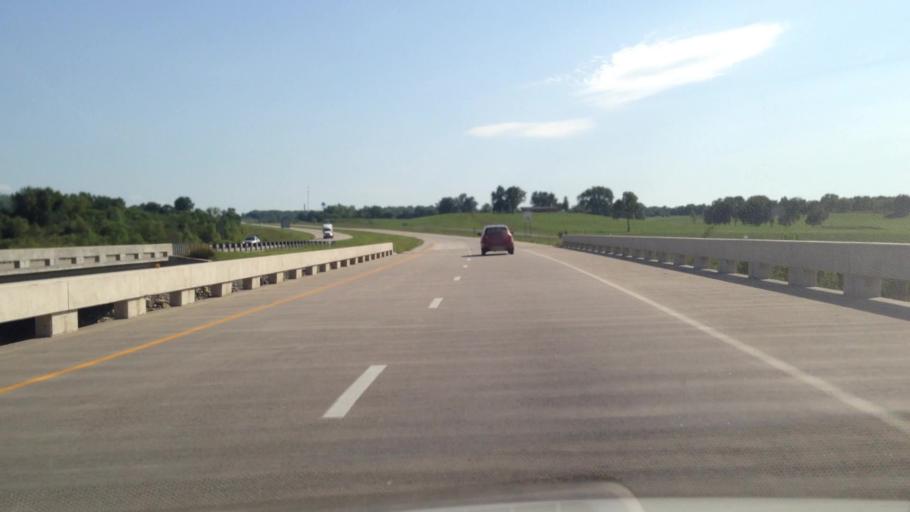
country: US
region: Kansas
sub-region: Linn County
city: Pleasanton
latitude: 38.1383
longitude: -94.7128
